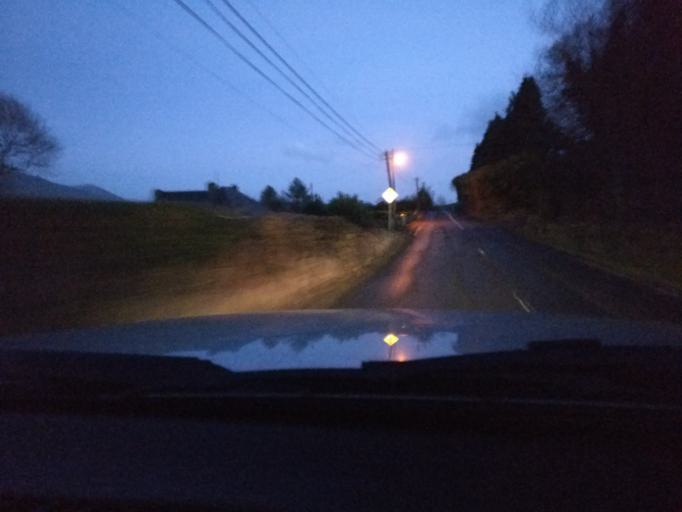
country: GB
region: Northern Ireland
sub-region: Down District
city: Warrenpoint
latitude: 54.0724
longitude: -6.2363
